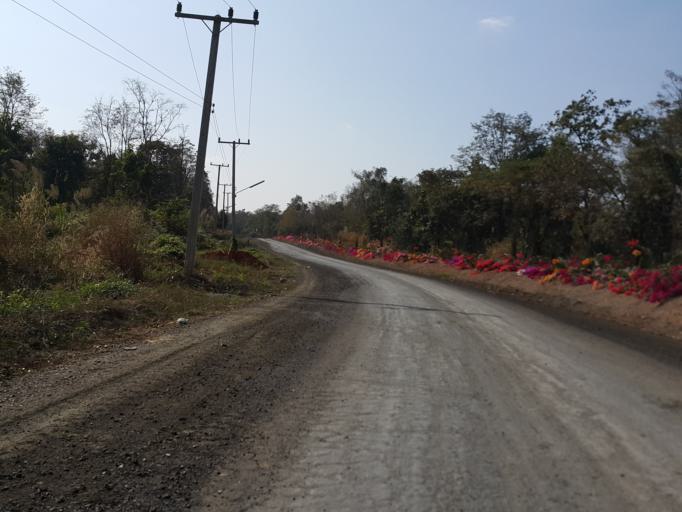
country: TH
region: Chiang Mai
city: Mae On
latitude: 18.8404
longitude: 99.2282
